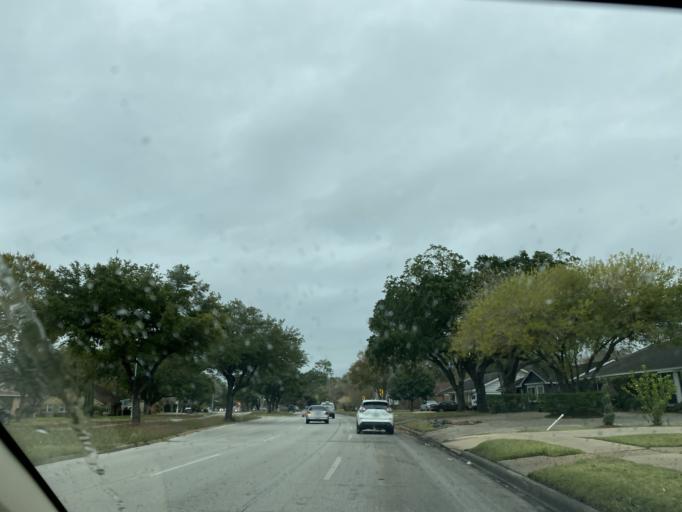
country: US
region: Texas
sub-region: Harris County
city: Piney Point Village
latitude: 29.7292
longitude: -95.5092
